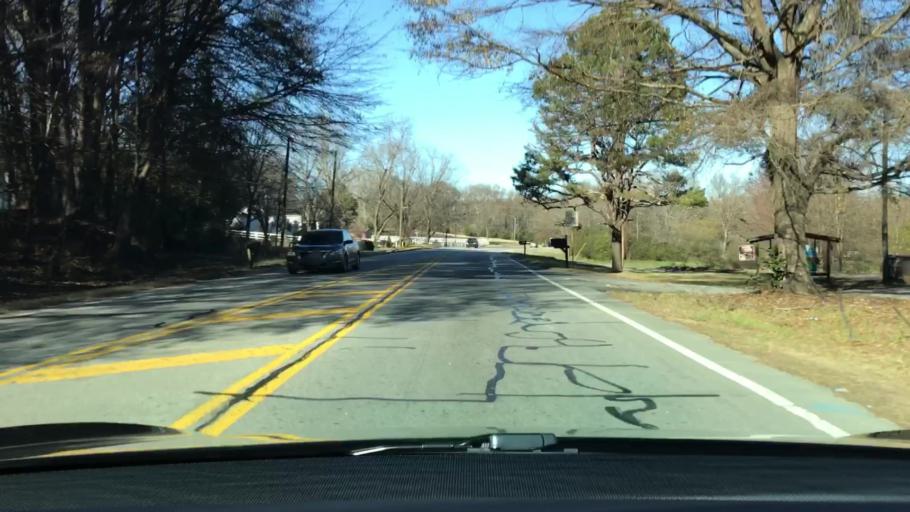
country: US
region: Georgia
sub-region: Barrow County
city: Russell
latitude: 33.9229
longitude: -83.7156
